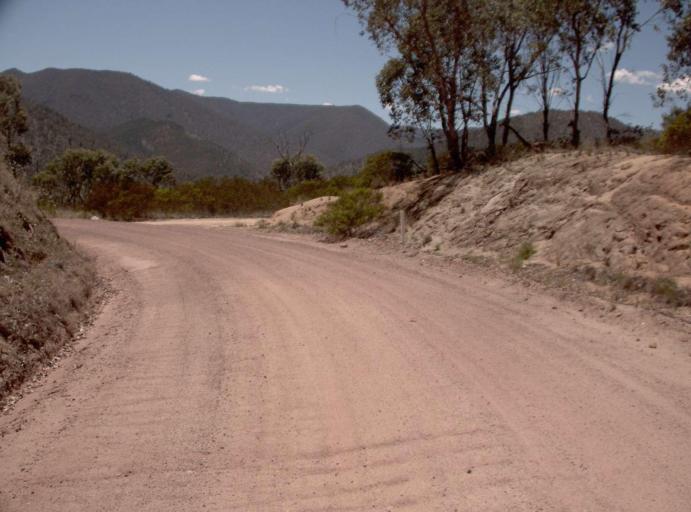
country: AU
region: New South Wales
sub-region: Snowy River
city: Jindabyne
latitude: -36.9218
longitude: 148.3957
